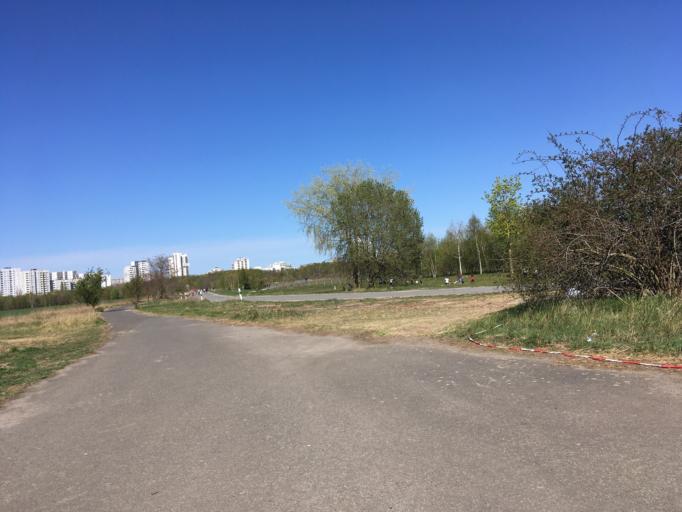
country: DE
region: Berlin
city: Gropiusstadt
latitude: 52.4125
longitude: 13.4608
